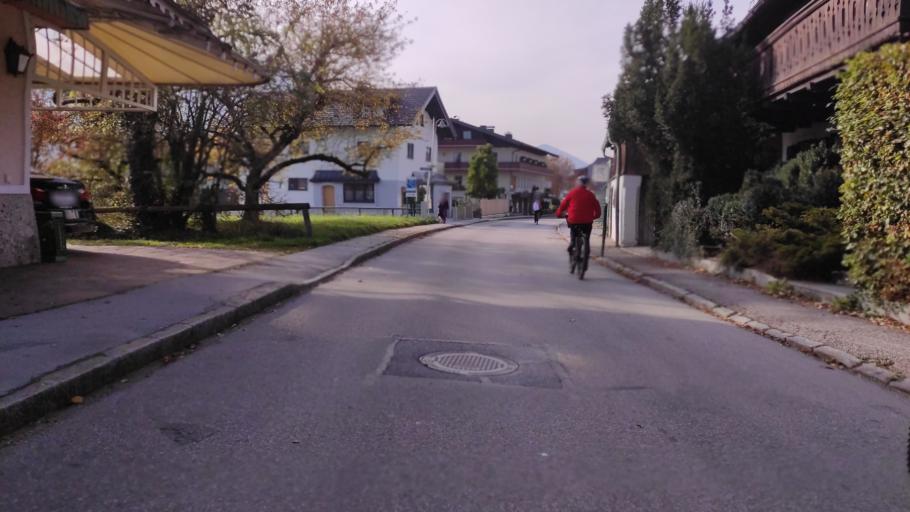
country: AT
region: Salzburg
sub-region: Politischer Bezirk Salzburg-Umgebung
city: Fuschl am See
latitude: 47.7965
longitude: 13.3018
